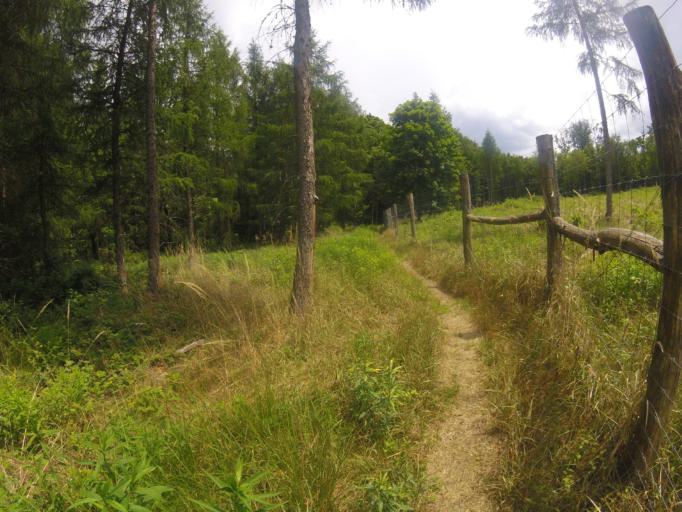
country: HU
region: Veszprem
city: Urkut
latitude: 47.0678
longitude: 17.6506
